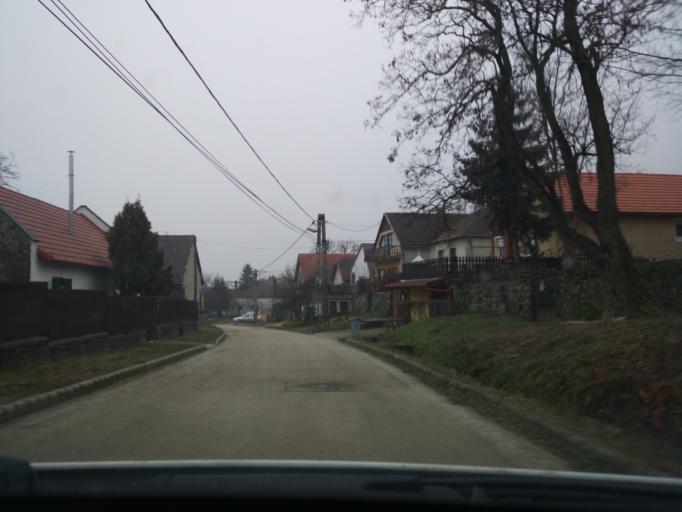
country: HU
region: Veszprem
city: Badacsonytomaj
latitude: 46.8088
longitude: 17.5115
